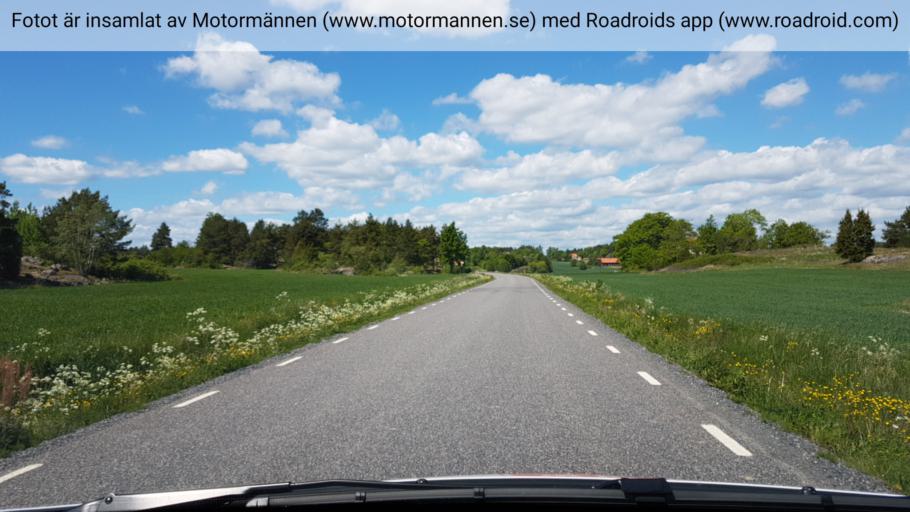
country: SE
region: Kalmar
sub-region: Vasterviks Kommun
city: Forserum
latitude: 58.0041
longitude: 16.5878
